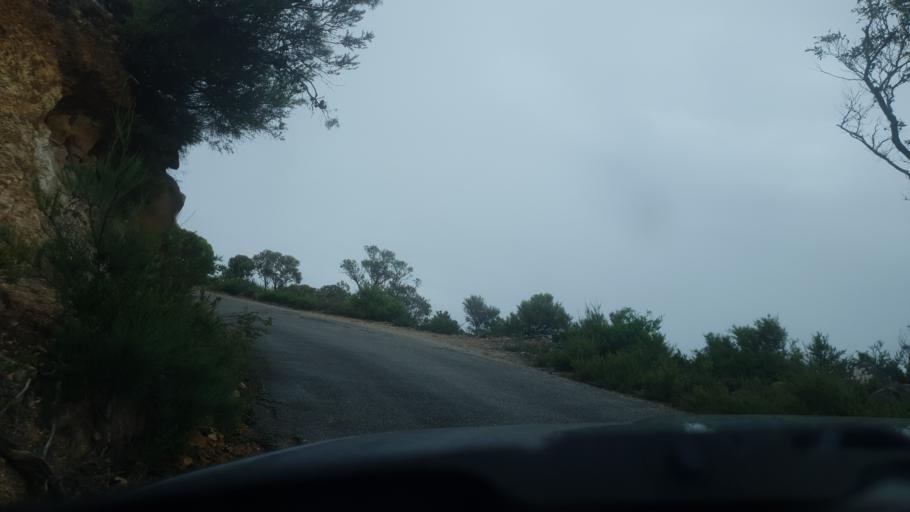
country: AU
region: Victoria
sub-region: Northern Grampians
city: Stawell
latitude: -37.2773
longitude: 142.5821
